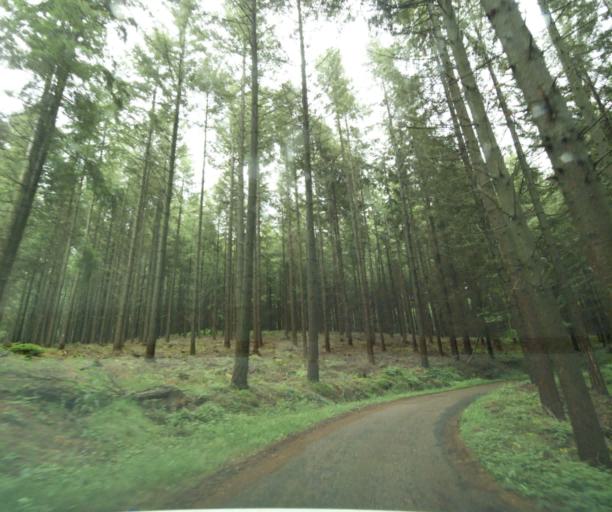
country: FR
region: Bourgogne
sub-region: Departement de Saone-et-Loire
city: Matour
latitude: 46.4486
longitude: 4.4676
